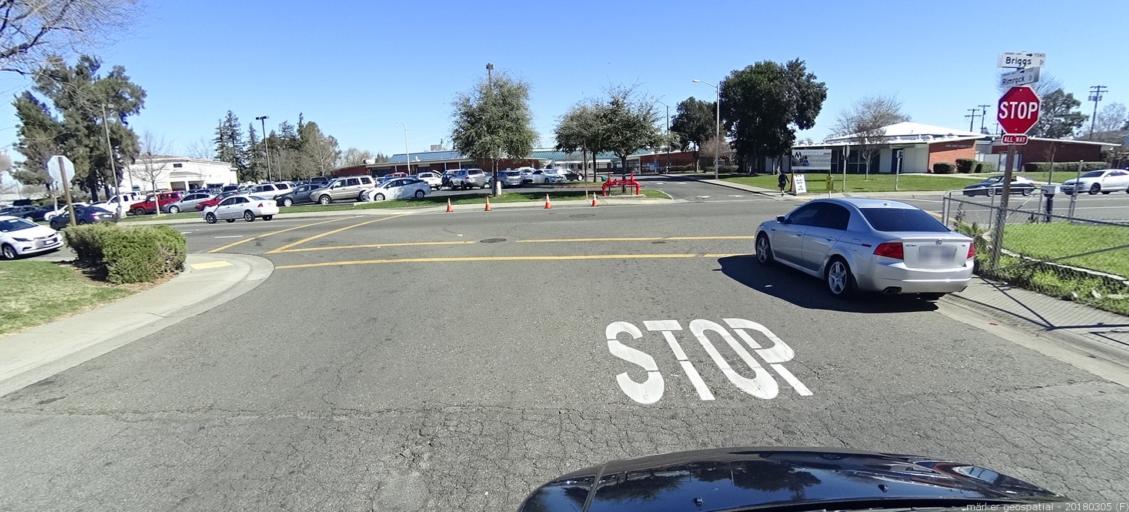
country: US
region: California
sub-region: Sacramento County
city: Florin
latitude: 38.4984
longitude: -121.4181
